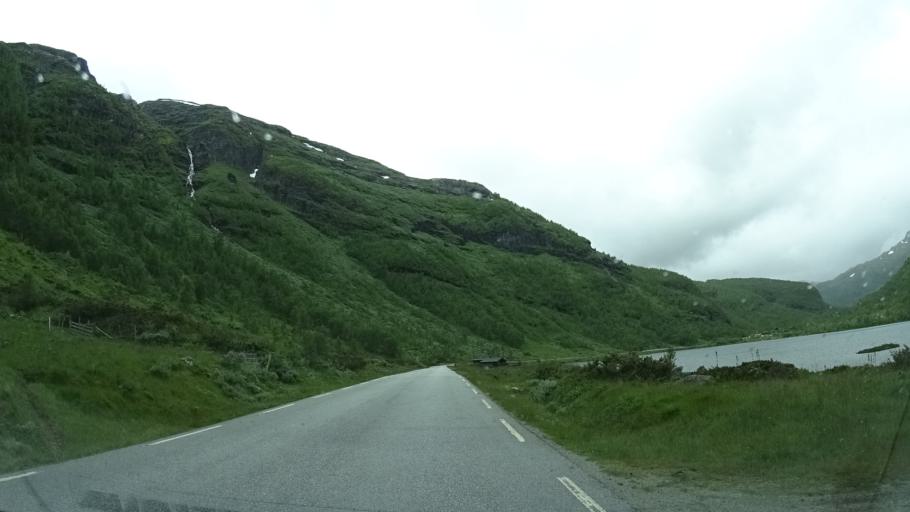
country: NO
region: Sogn og Fjordane
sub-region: Laerdal
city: Laerdalsoyri
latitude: 60.8248
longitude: 7.5054
